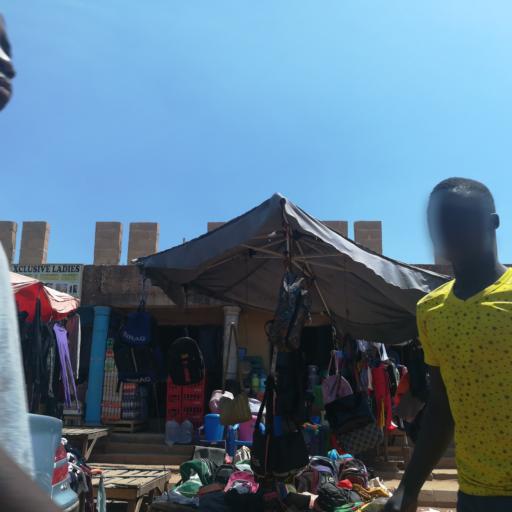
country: NG
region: Plateau
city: Bukuru
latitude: 9.7907
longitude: 8.8646
